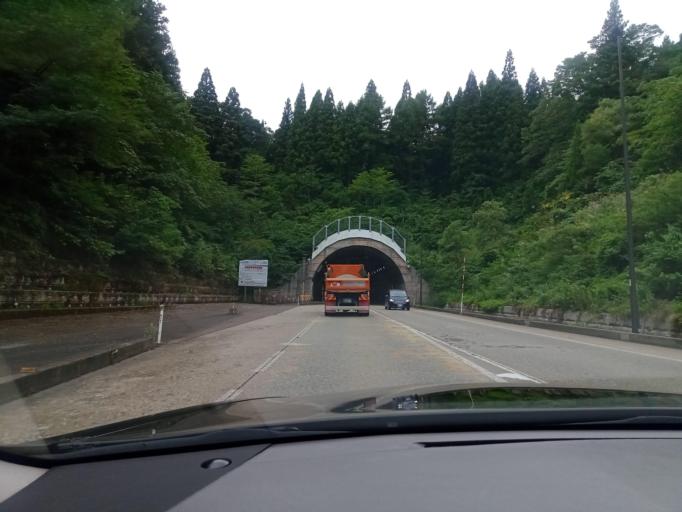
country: JP
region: Niigata
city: Arai
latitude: 36.8736
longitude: 138.2010
